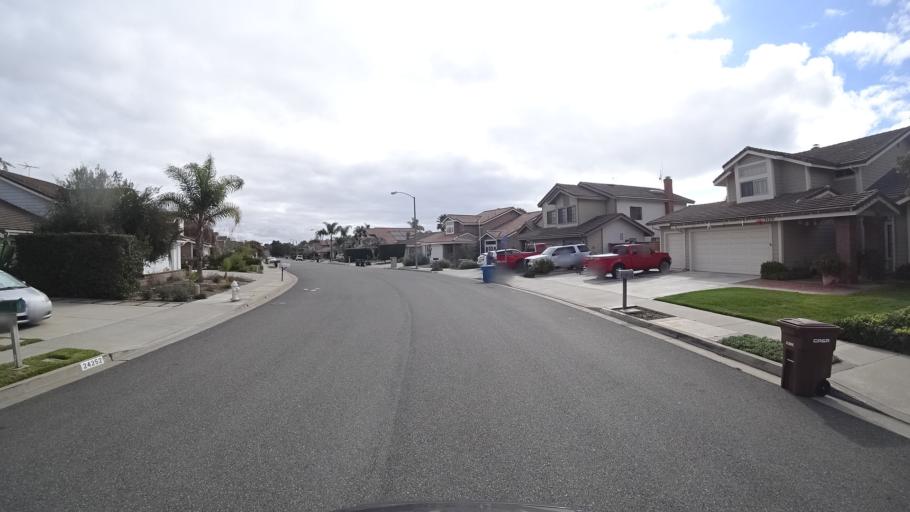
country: US
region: California
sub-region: Orange County
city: Dana Point
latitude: 33.4862
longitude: -117.7062
